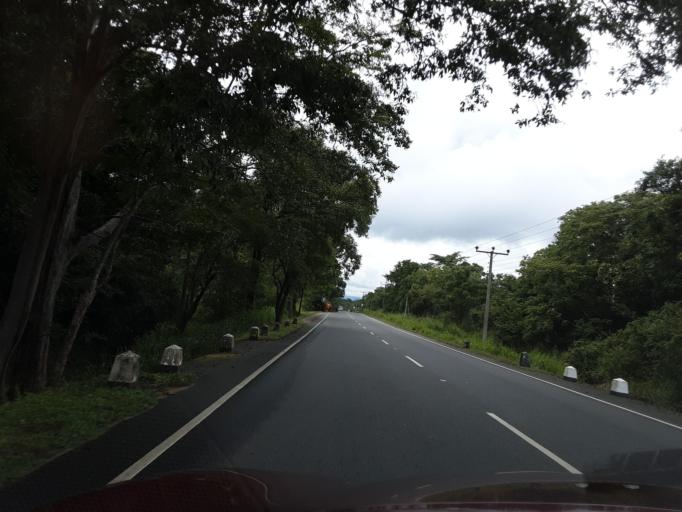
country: LK
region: Uva
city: Badulla
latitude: 7.3982
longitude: 81.1097
